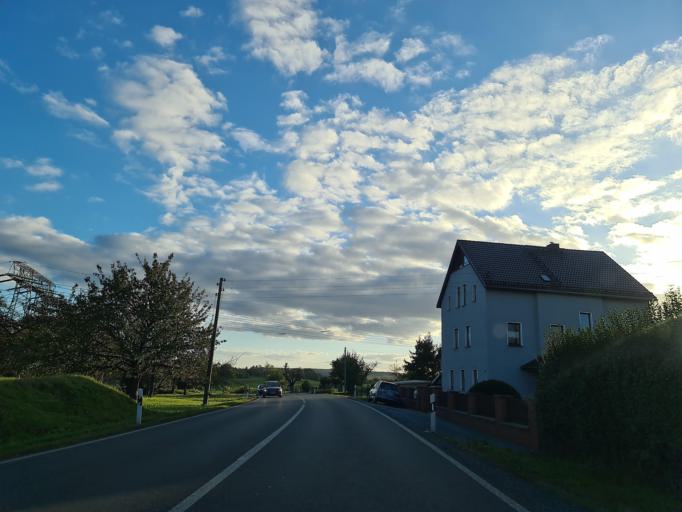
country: DE
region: Thuringia
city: Crimla
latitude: 50.7947
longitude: 12.0614
